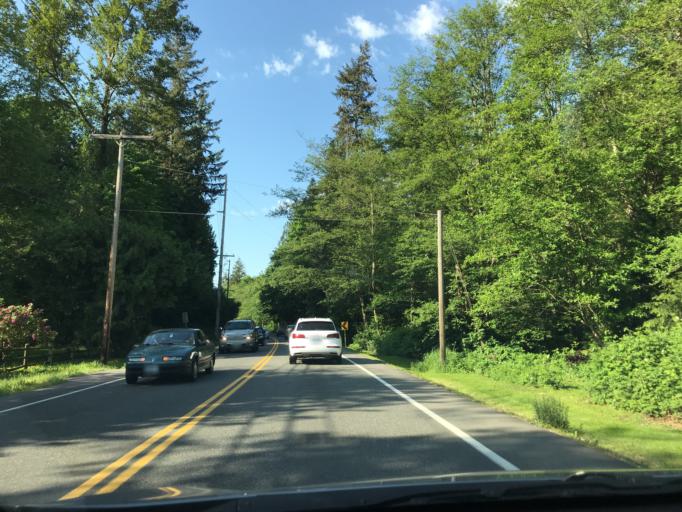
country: US
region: Washington
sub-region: King County
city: Issaquah
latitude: 47.4940
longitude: -122.0225
